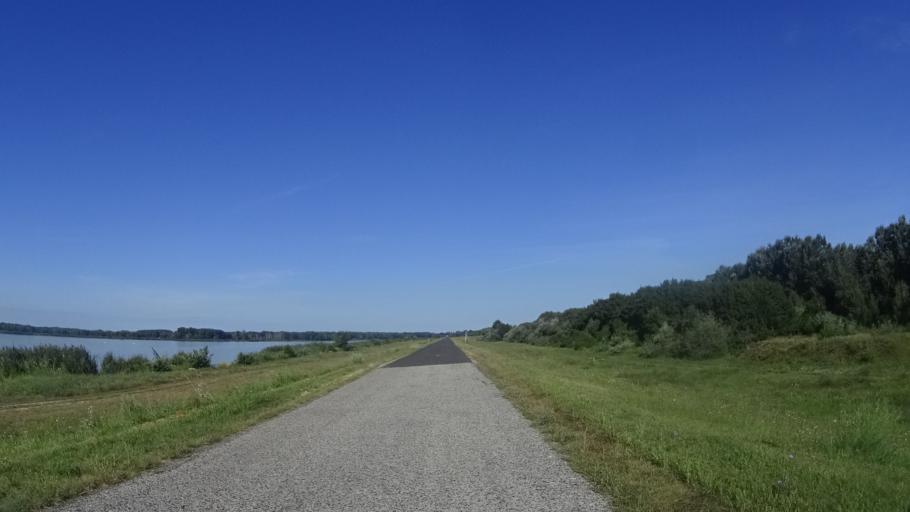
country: SK
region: Bratislavsky
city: Dunajska Luzna
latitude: 48.0597
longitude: 17.2087
